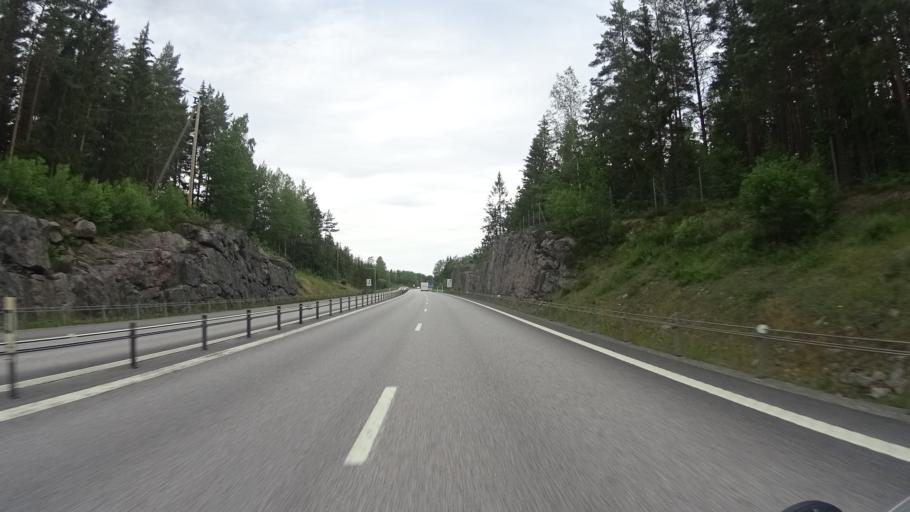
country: SE
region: OEstergoetland
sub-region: Valdemarsviks Kommun
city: Gusum
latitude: 58.2633
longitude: 16.5228
